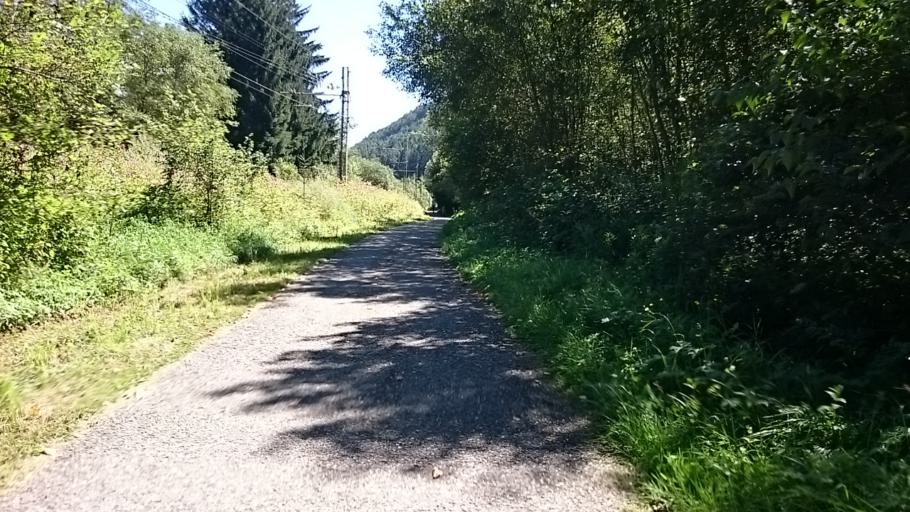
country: IT
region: Trentino-Alto Adige
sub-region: Bolzano
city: Terento
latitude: 46.8067
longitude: 11.8063
